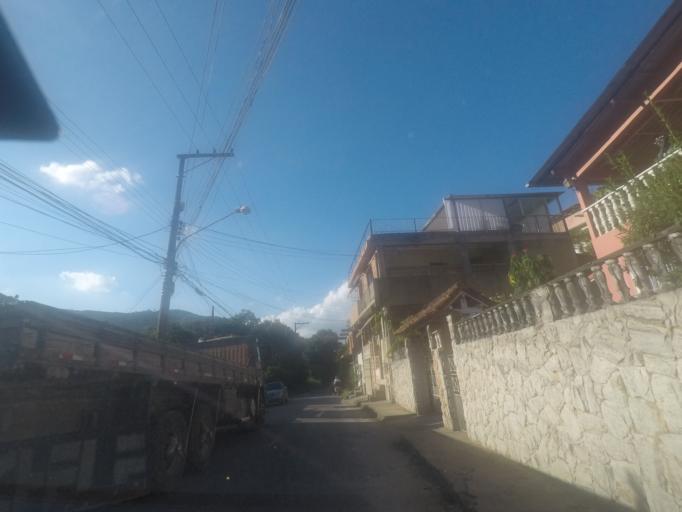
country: BR
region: Rio de Janeiro
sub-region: Petropolis
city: Petropolis
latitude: -22.4939
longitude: -43.1494
